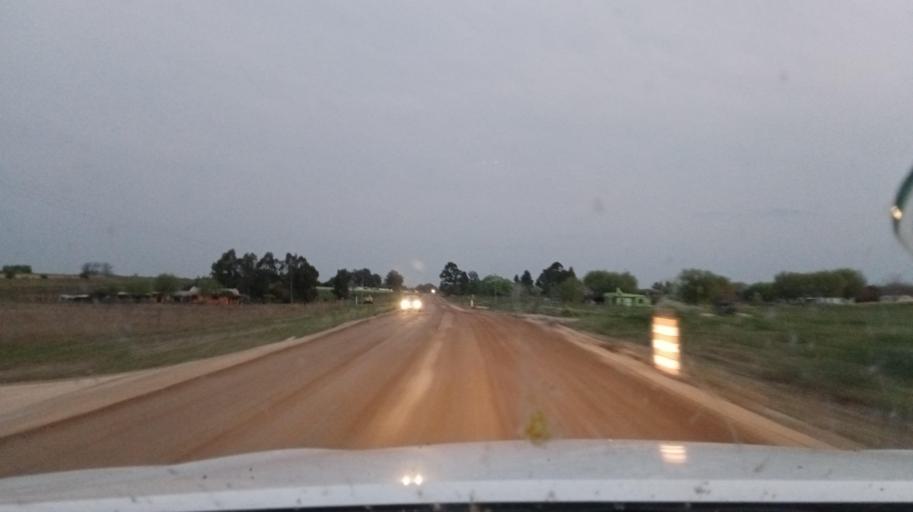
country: UY
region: Canelones
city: Santa Rosa
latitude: -34.5468
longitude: -56.1018
